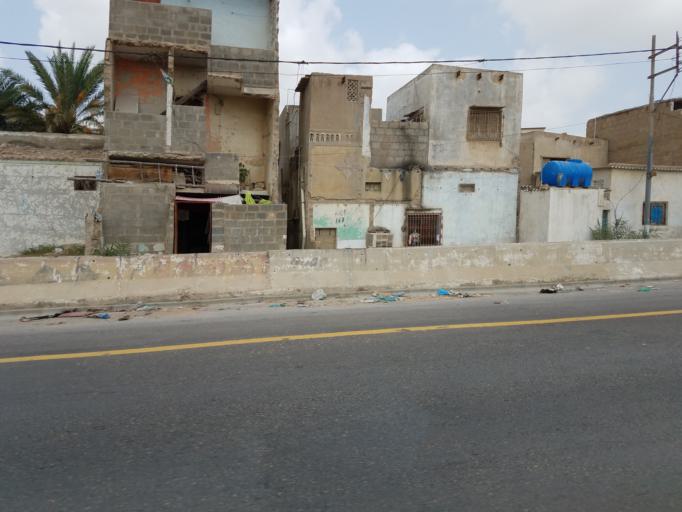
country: PK
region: Sindh
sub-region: Karachi District
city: Karachi
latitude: 24.8939
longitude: 67.0399
